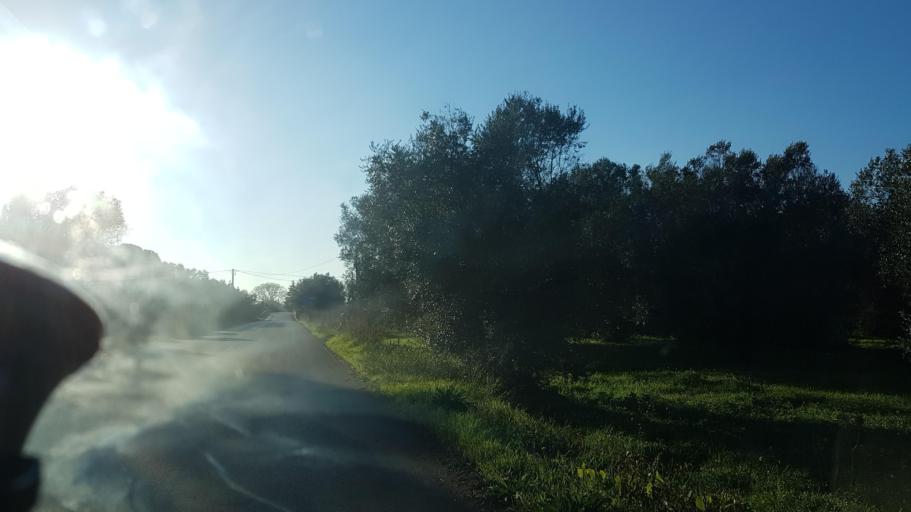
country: IT
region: Apulia
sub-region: Provincia di Brindisi
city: Latiano
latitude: 40.5631
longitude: 17.7350
